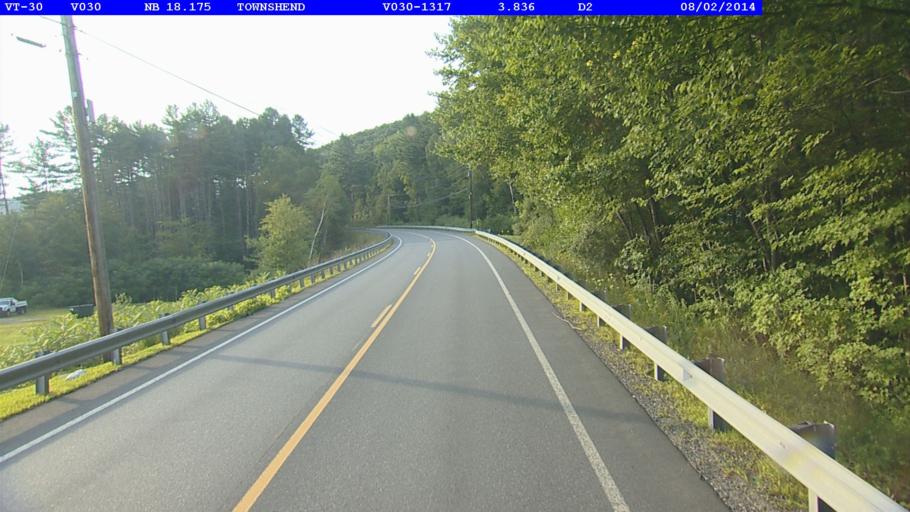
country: US
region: Vermont
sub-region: Windham County
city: Newfane
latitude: 43.0516
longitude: -72.6977
